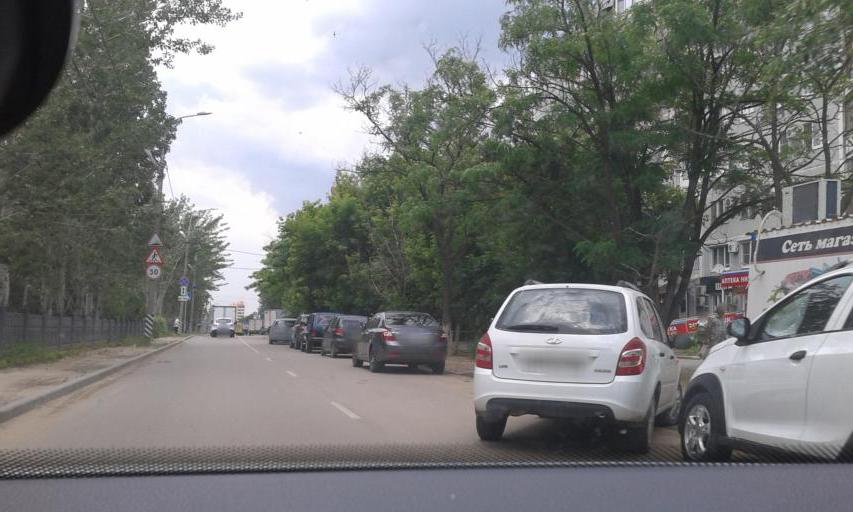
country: RU
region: Volgograd
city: Volgograd
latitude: 48.7549
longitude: 44.5032
